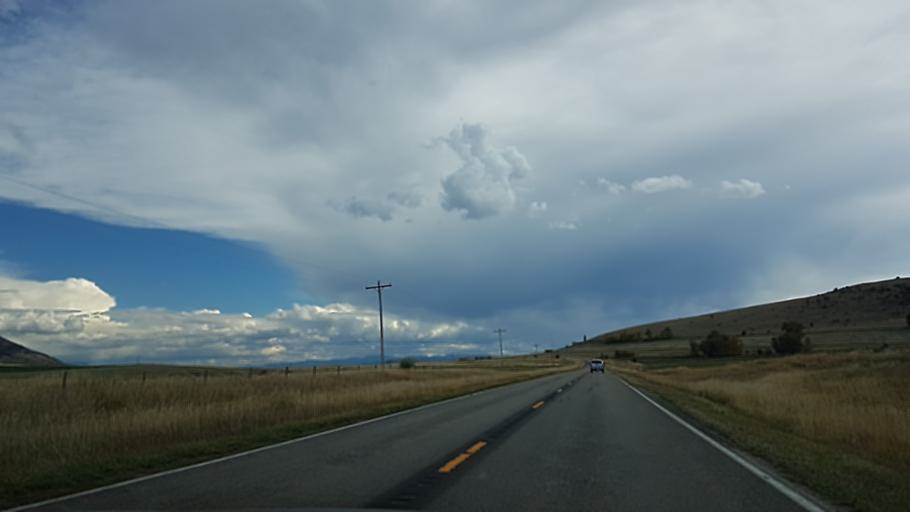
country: US
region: Montana
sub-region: Jefferson County
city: Whitehall
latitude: 45.7824
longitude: -111.9144
